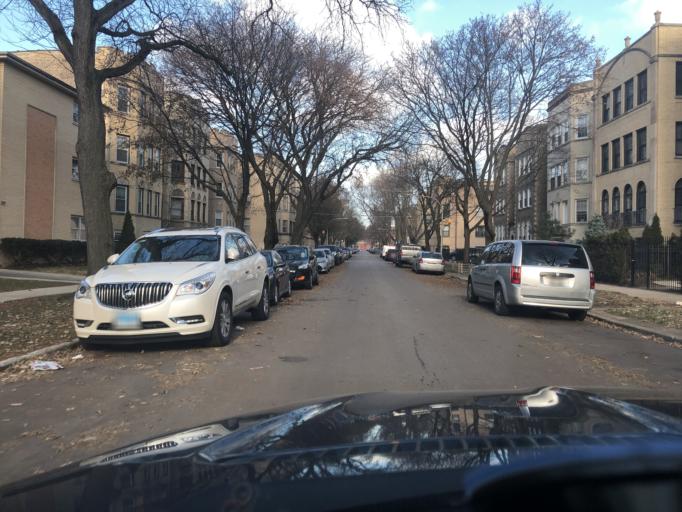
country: US
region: Illinois
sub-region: Cook County
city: Evanston
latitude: 42.0152
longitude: -87.6817
